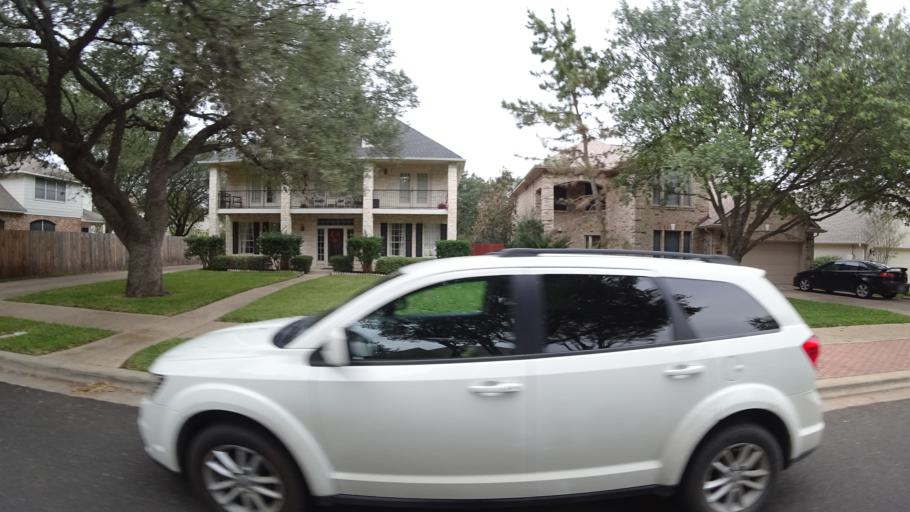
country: US
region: Texas
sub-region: Travis County
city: Shady Hollow
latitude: 30.1869
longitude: -97.8838
